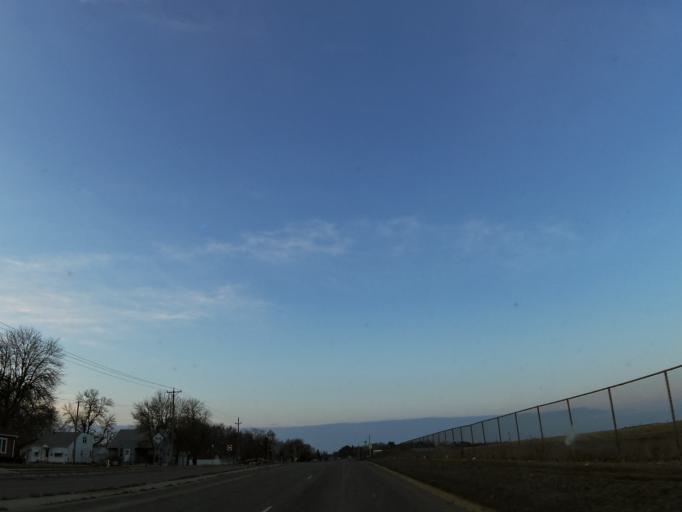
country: US
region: Minnesota
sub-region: Mower County
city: Austin
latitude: 43.6672
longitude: -92.9394
